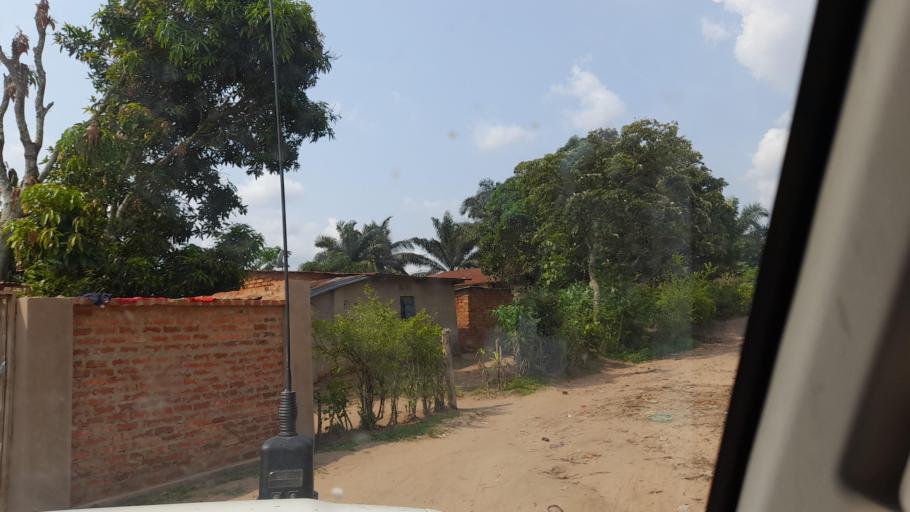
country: CD
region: Kasai-Occidental
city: Kananga
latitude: -5.9059
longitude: 22.4748
